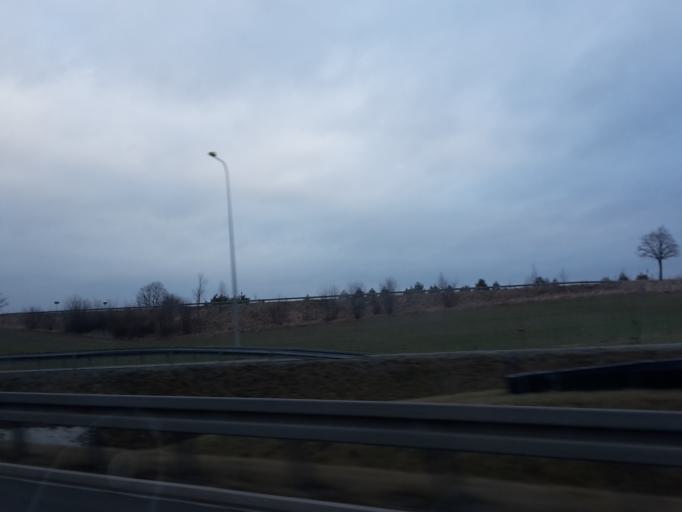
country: PL
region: Warmian-Masurian Voivodeship
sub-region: Powiat ostrodzki
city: Milomlyn
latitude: 53.8075
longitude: 19.7868
